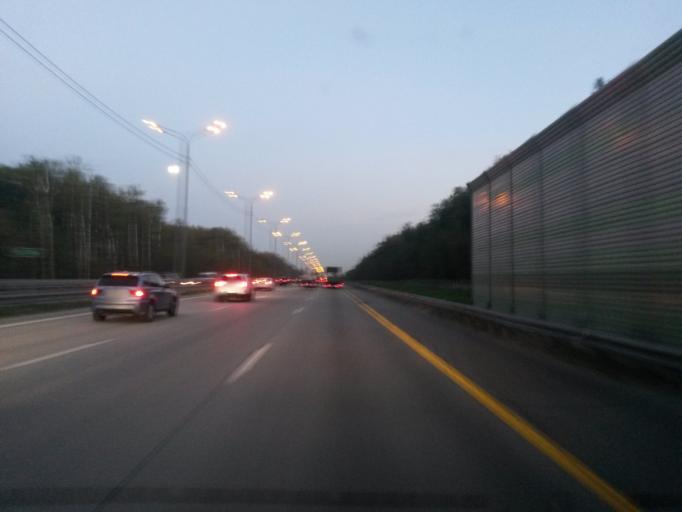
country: RU
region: Moskovskaya
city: Belyye Stolby
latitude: 55.3040
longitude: 37.8322
